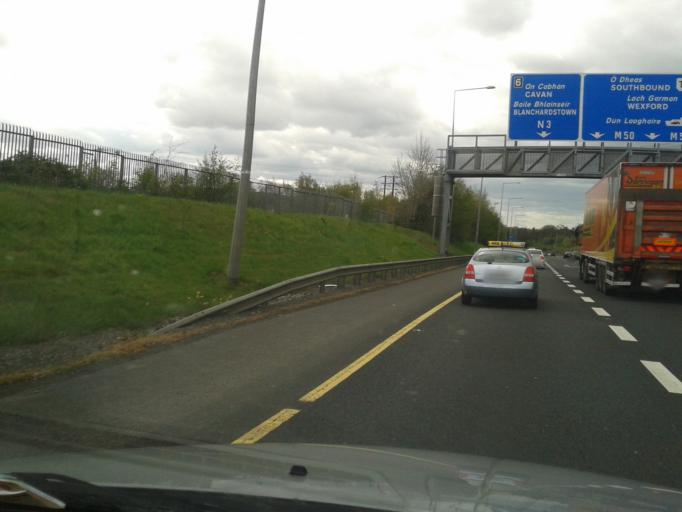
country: IE
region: Leinster
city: Castleknock
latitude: 53.3901
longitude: -6.3497
